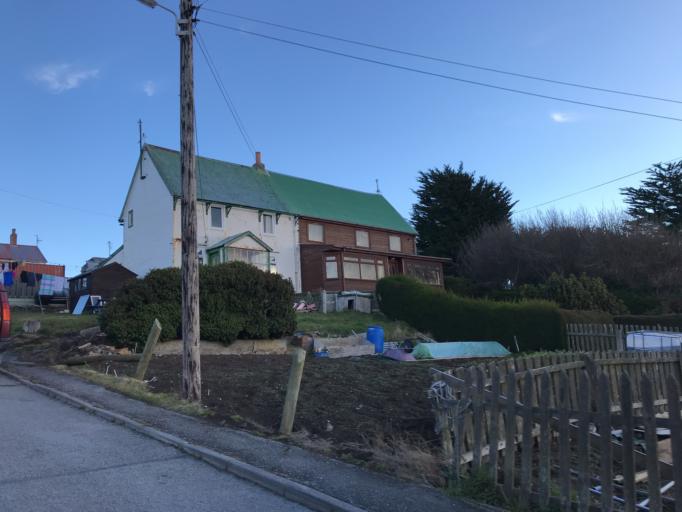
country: FK
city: Stanley
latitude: -51.6935
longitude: -57.8622
